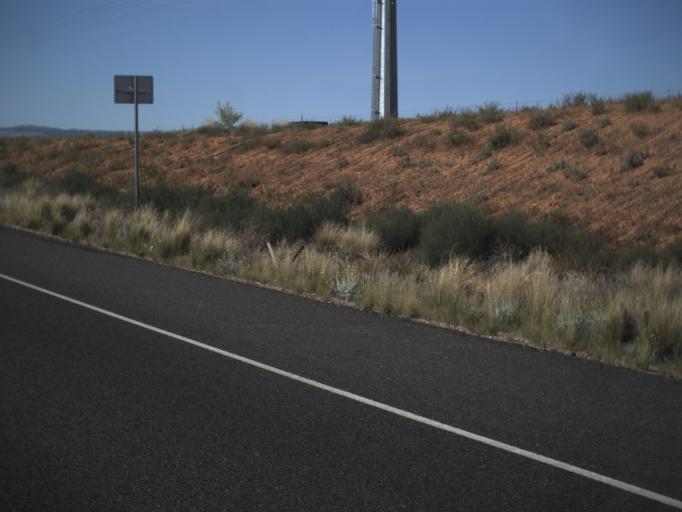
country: US
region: Utah
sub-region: Washington County
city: Washington
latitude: 37.0158
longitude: -113.4948
